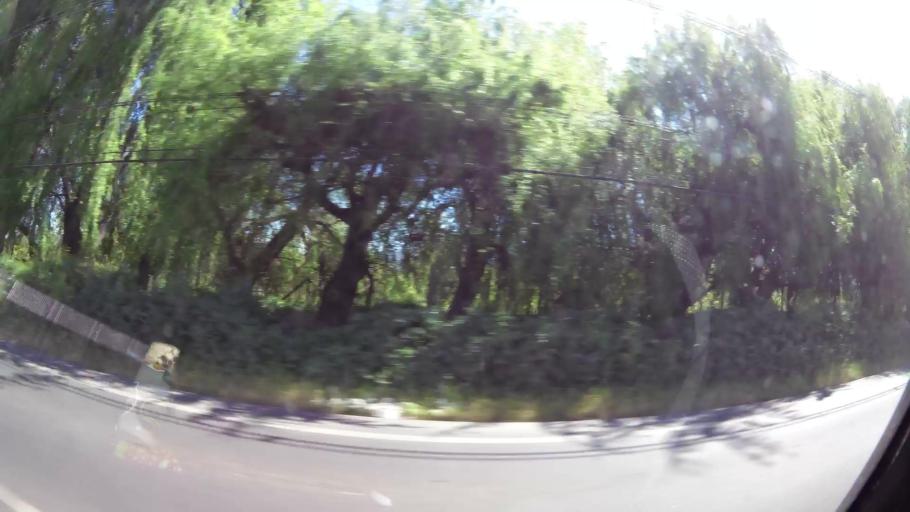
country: CL
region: Santiago Metropolitan
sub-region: Provincia de Talagante
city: Penaflor
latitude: -33.6194
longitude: -70.9079
